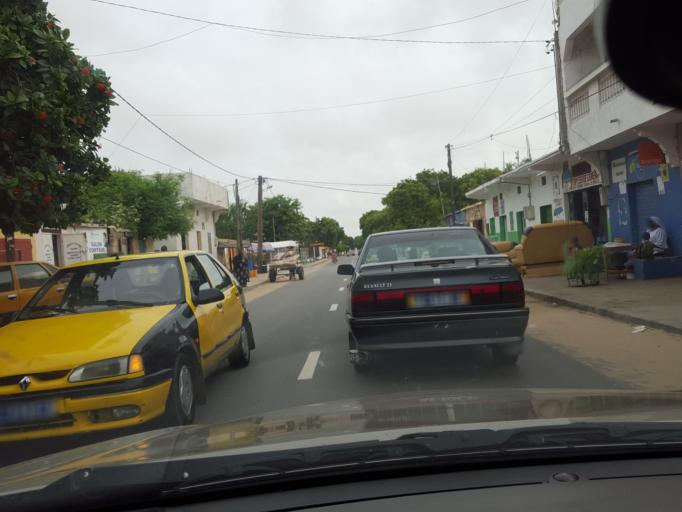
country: SN
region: Saint-Louis
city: Saint-Louis
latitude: 16.0292
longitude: -16.4889
